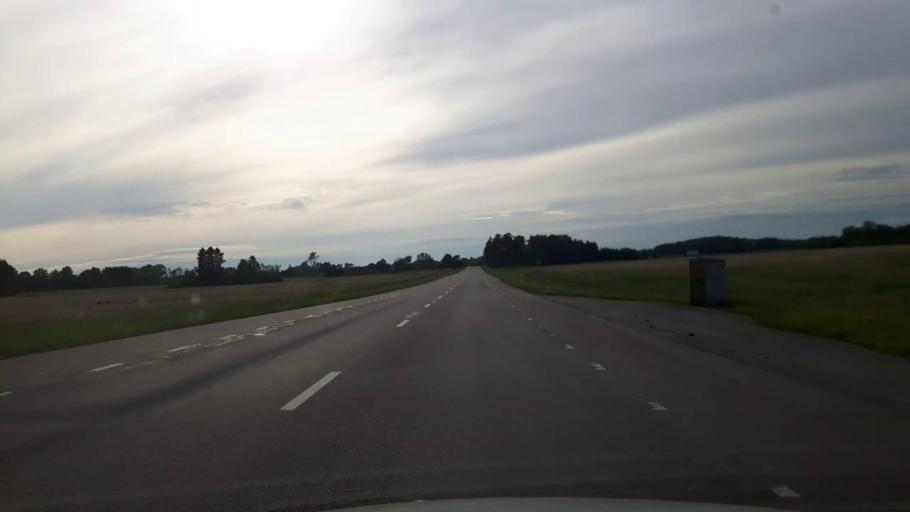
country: SE
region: Uppsala
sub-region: Enkopings Kommun
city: Orsundsbro
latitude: 59.6535
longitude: 17.3607
